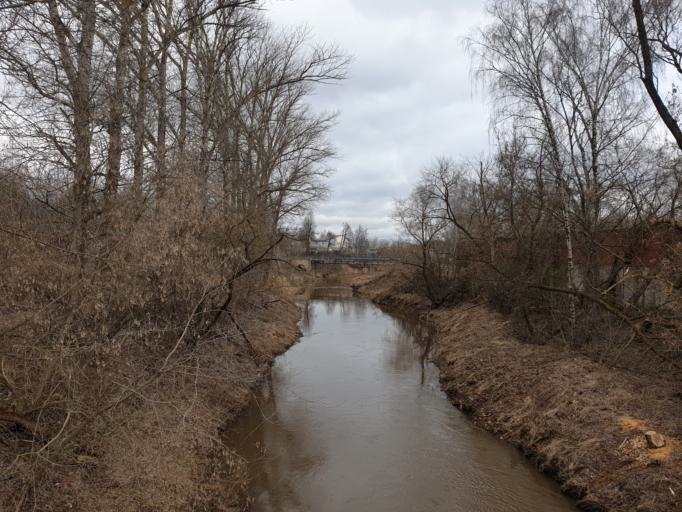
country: RU
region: Kostroma
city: Nerekhta
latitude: 57.4633
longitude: 40.5814
